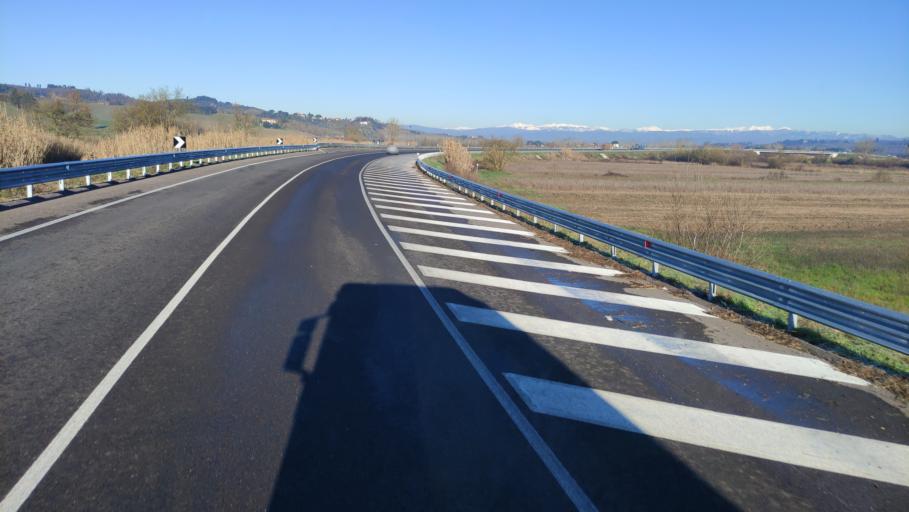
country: IT
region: Tuscany
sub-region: Province of Pisa
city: Ponte A Elsa
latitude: 43.6527
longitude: 10.9271
